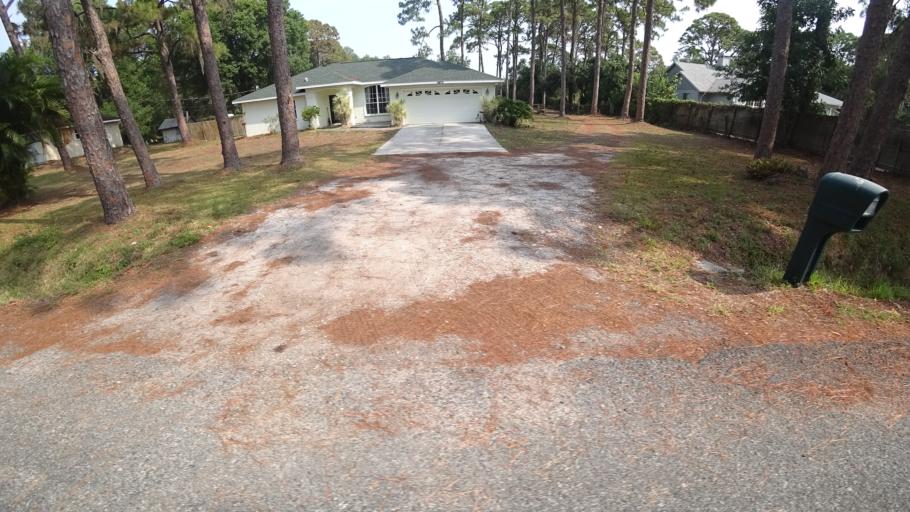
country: US
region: Florida
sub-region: Manatee County
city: Samoset
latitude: 27.4730
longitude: -82.4994
